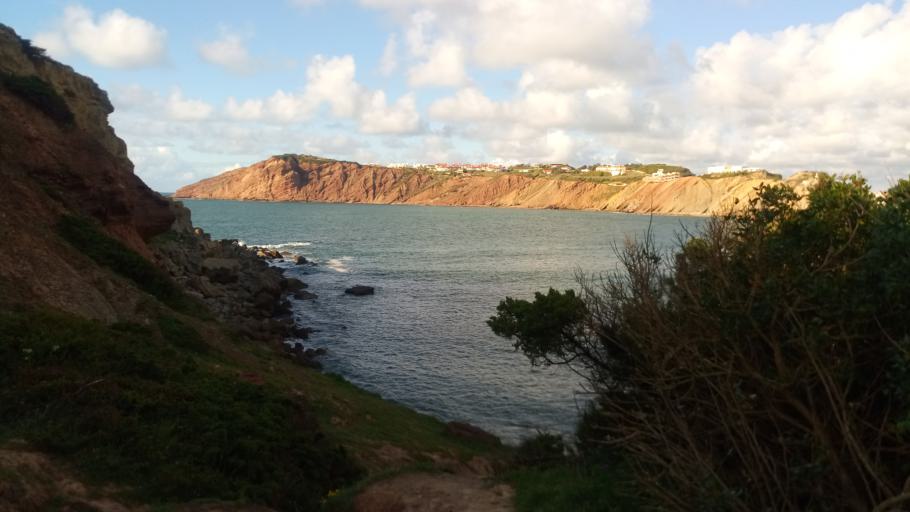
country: PT
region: Leiria
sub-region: Caldas da Rainha
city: Caldas da Rainha
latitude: 39.5082
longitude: -9.1484
